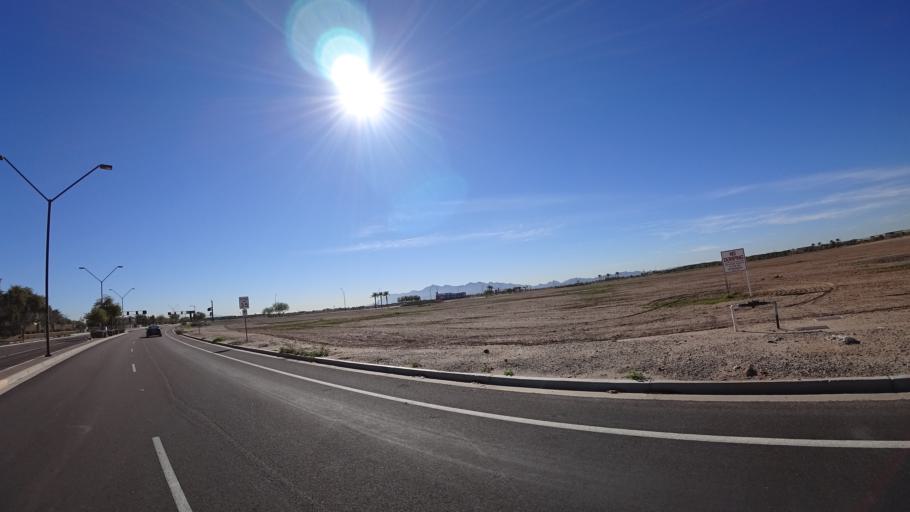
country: US
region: Arizona
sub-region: Maricopa County
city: Litchfield Park
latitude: 33.4749
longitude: -112.3849
